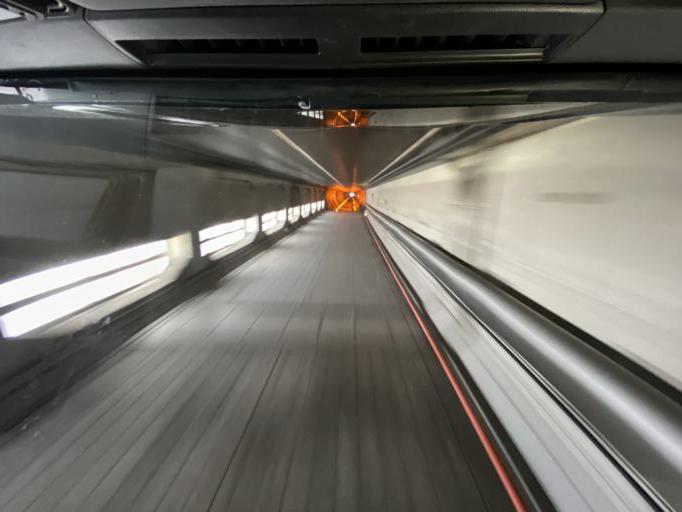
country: JP
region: Hokkaido
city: Rumoi
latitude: 43.7966
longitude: 141.3767
